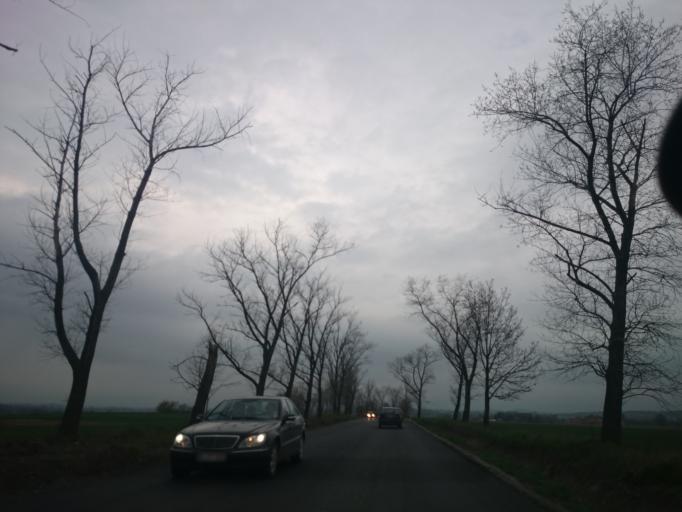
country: PL
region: Lower Silesian Voivodeship
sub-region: Powiat zabkowicki
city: Kamieniec Zabkowicki
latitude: 50.5555
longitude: 16.8546
